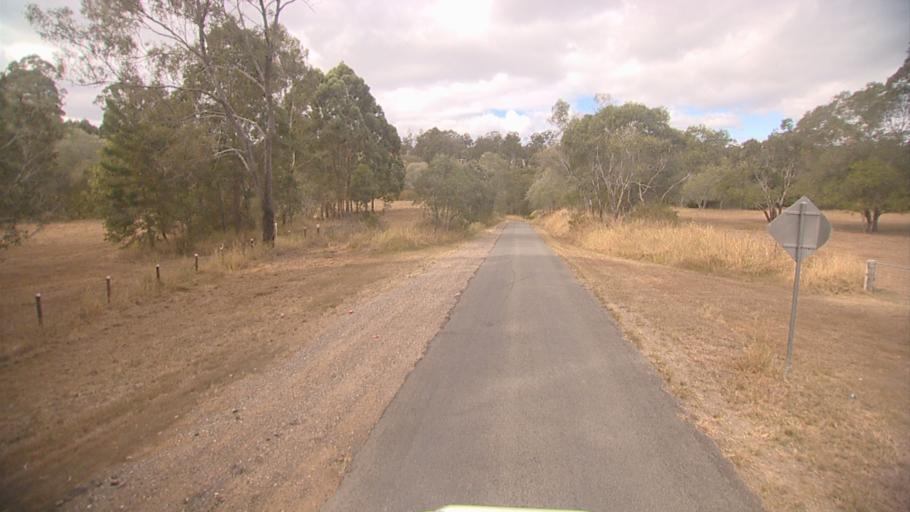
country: AU
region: Queensland
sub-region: Logan
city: Cedar Vale
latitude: -27.8871
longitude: 153.0242
